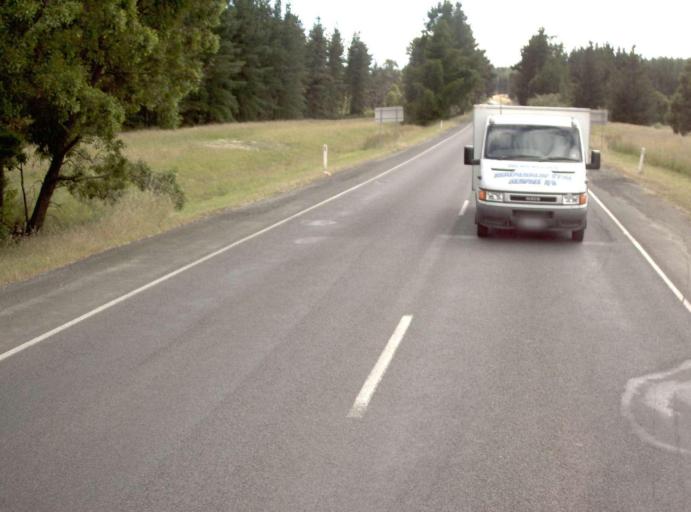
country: AU
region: Victoria
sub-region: Latrobe
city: Morwell
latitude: -38.1994
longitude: 146.4405
